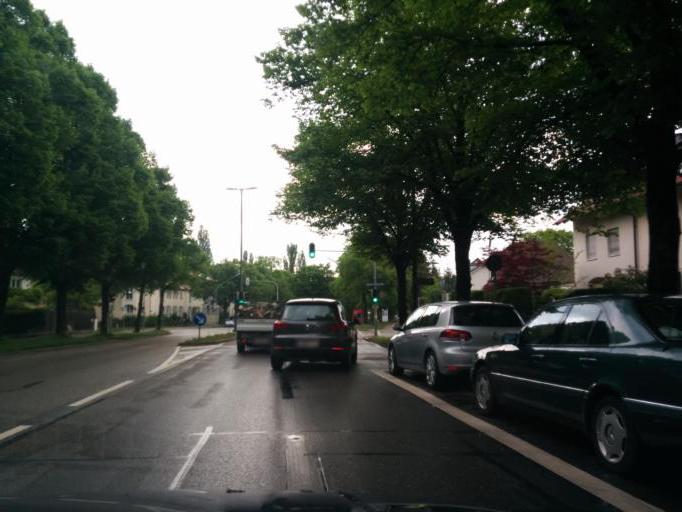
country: DE
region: Bavaria
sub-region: Upper Bavaria
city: Bogenhausen
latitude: 48.1167
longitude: 11.6243
